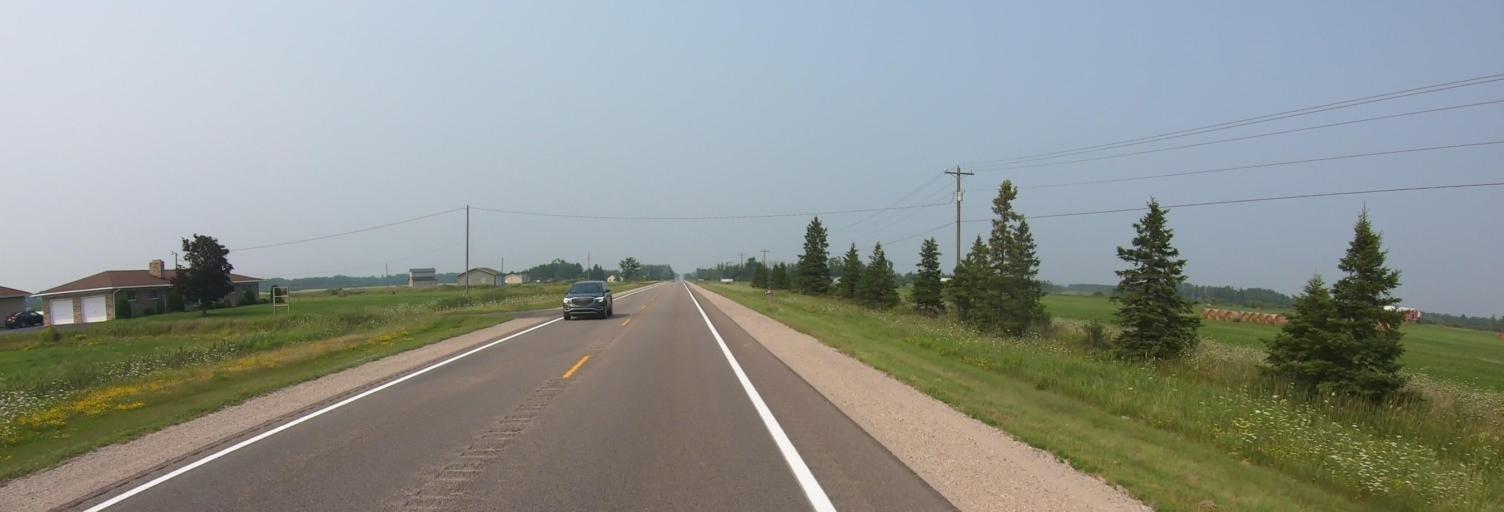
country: US
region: Michigan
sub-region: Chippewa County
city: Sault Ste. Marie
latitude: 46.1701
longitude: -84.3635
